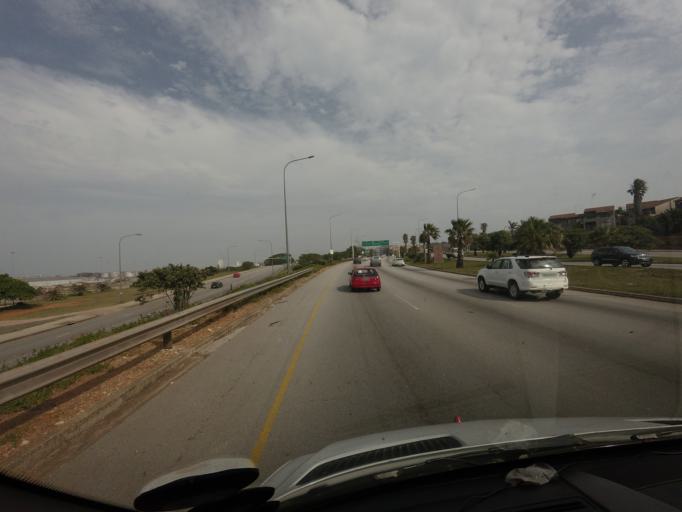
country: ZA
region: Eastern Cape
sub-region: Nelson Mandela Bay Metropolitan Municipality
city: Port Elizabeth
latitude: -33.9663
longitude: 25.6278
